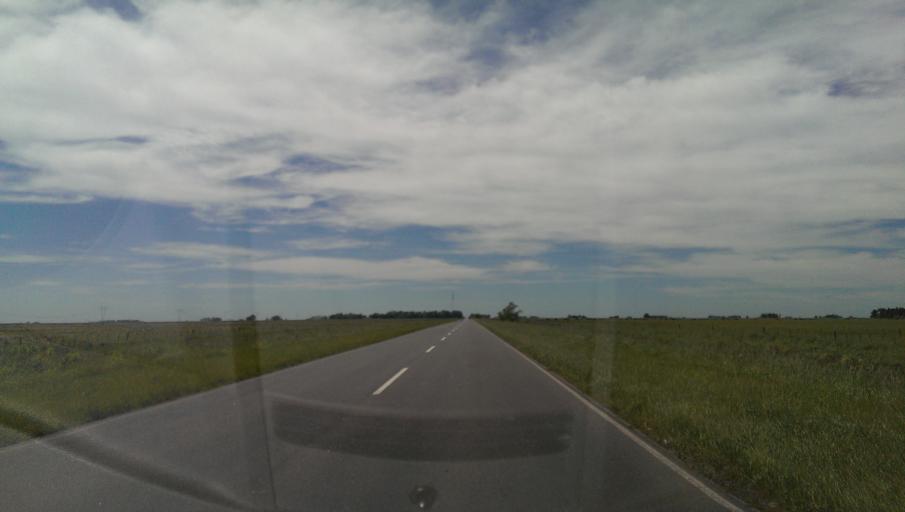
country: AR
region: Buenos Aires
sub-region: Partido de Laprida
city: Laprida
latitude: -37.2049
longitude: -60.6762
